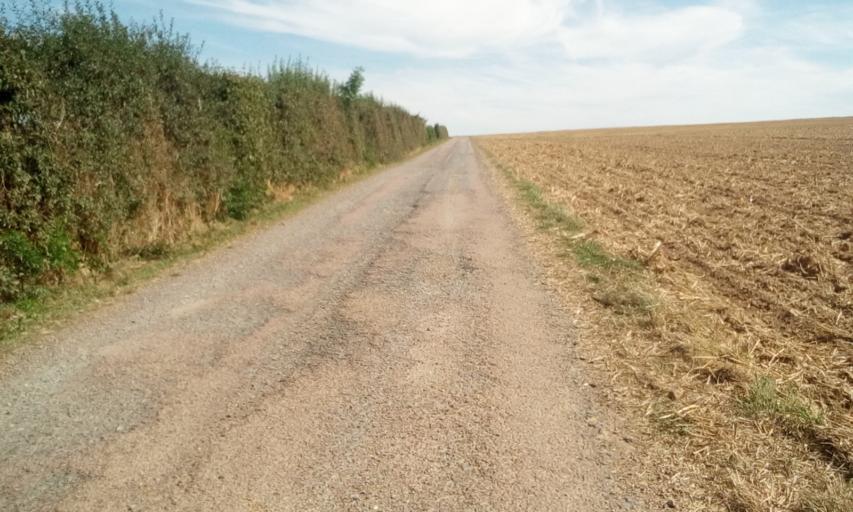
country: FR
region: Lower Normandy
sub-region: Departement du Calvados
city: Bretteville-sur-Odon
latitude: 49.1540
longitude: -0.4122
